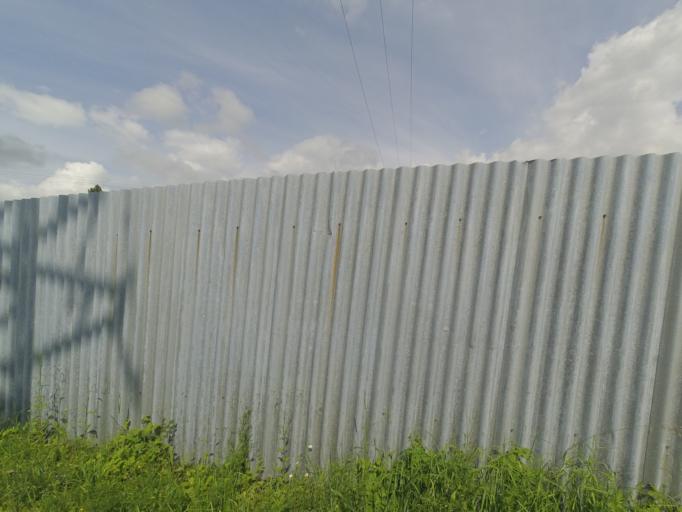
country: CZ
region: Karlovarsky
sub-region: Okres Cheb
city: Cheb
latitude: 50.0832
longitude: 12.4148
